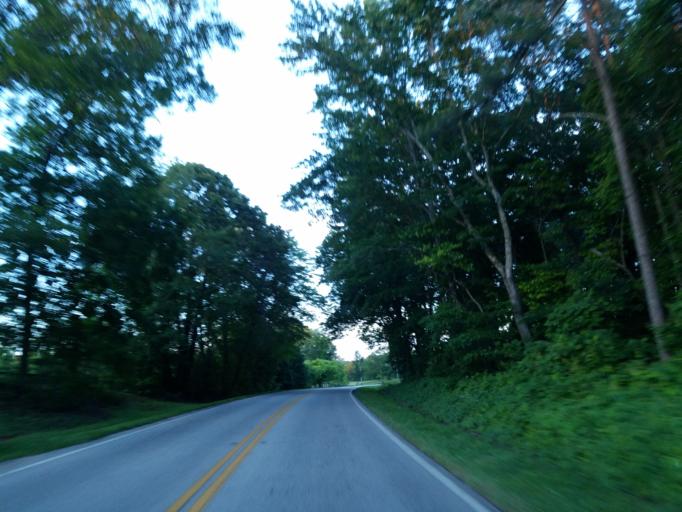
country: US
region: Georgia
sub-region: Lumpkin County
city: Dahlonega
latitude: 34.5609
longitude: -83.9097
